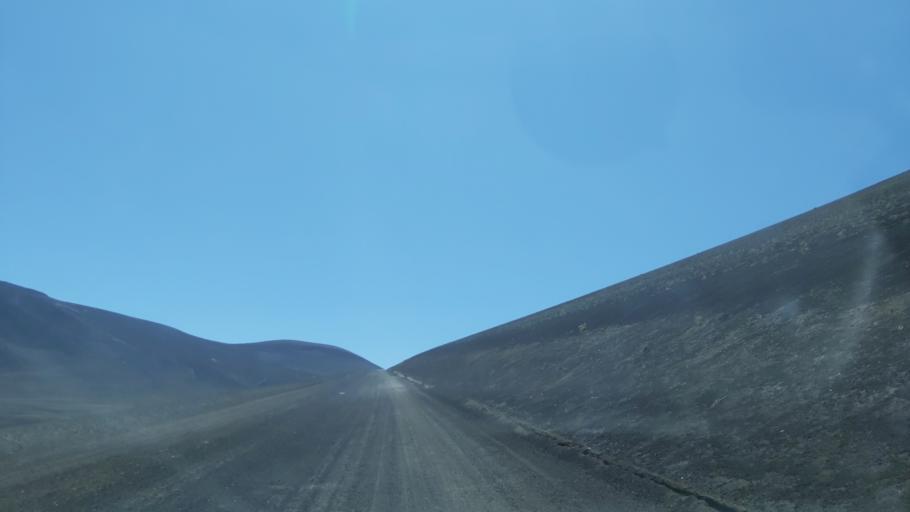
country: CL
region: Araucania
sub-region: Provincia de Cautin
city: Vilcun
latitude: -38.4022
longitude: -71.5445
